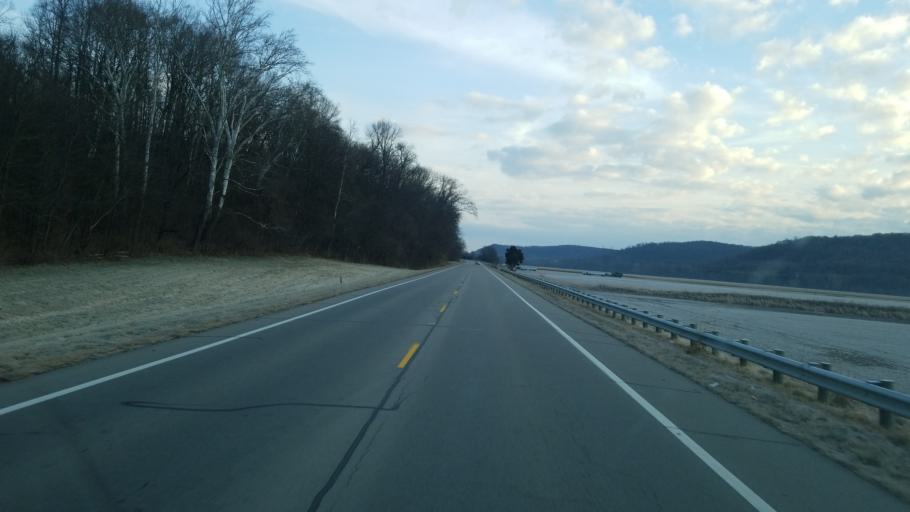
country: US
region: Ohio
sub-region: Ross County
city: North Fork Village
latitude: 39.3157
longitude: -83.1095
